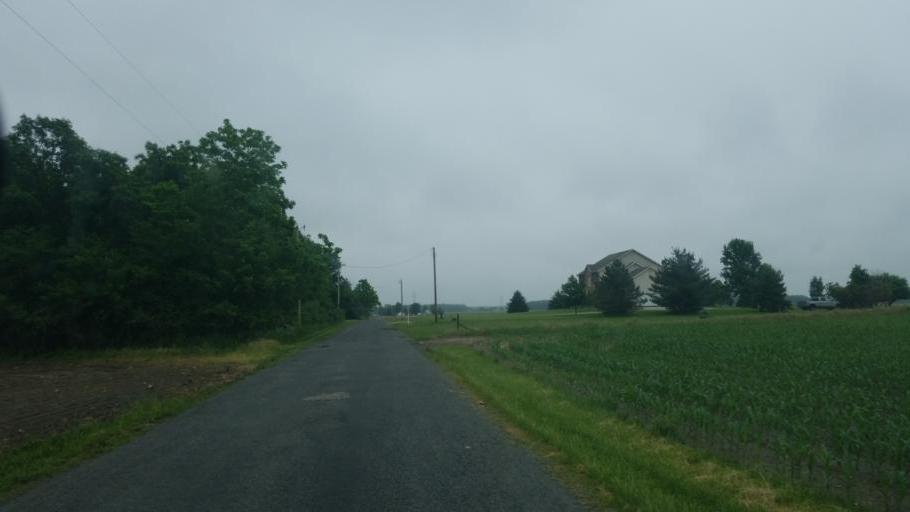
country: US
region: Indiana
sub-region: Marshall County
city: Bremen
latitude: 41.4792
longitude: -86.1471
